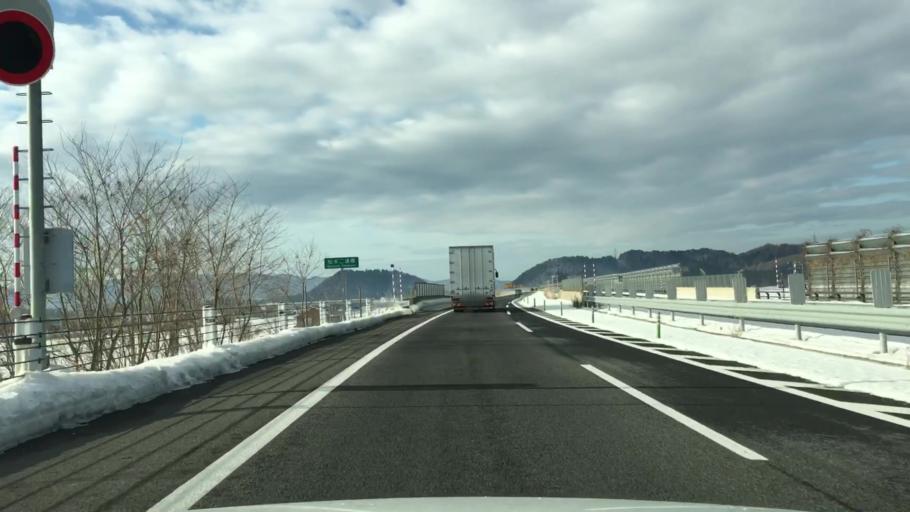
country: JP
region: Akita
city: Odate
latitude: 40.2911
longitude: 140.5496
